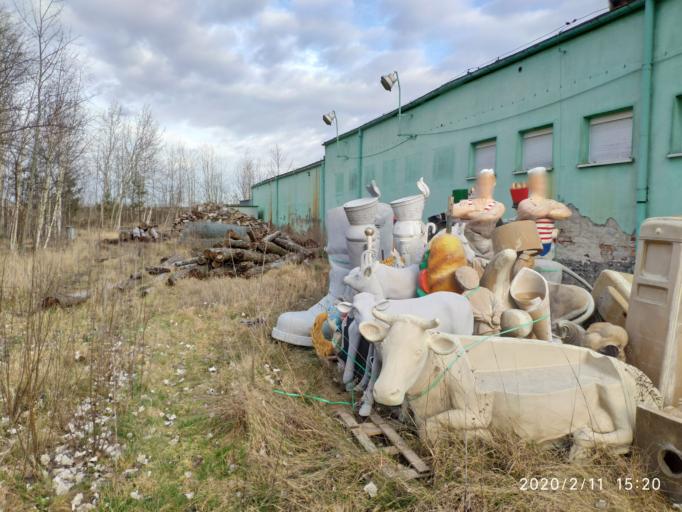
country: PL
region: Lubusz
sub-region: Powiat nowosolski
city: Nowa Sol
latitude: 51.8151
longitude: 15.7155
